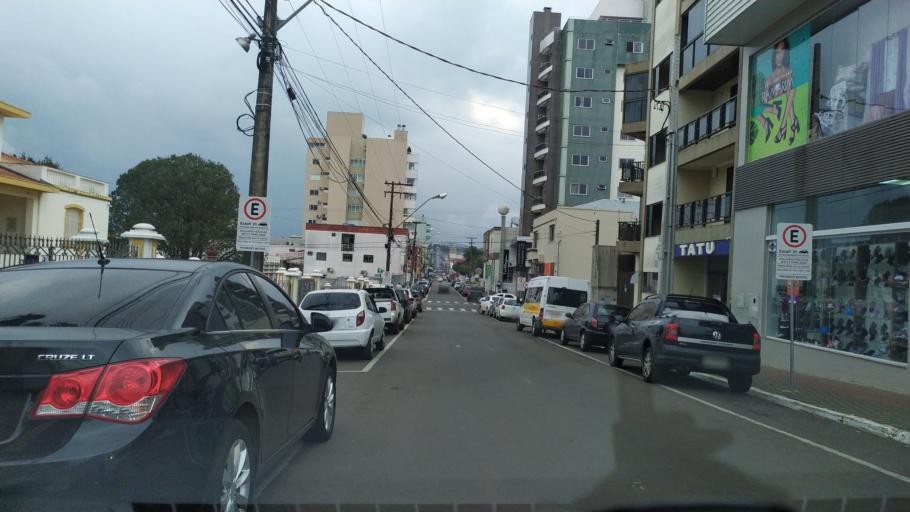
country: BR
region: Parana
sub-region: Palmas
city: Palmas
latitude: -26.4845
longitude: -51.9898
